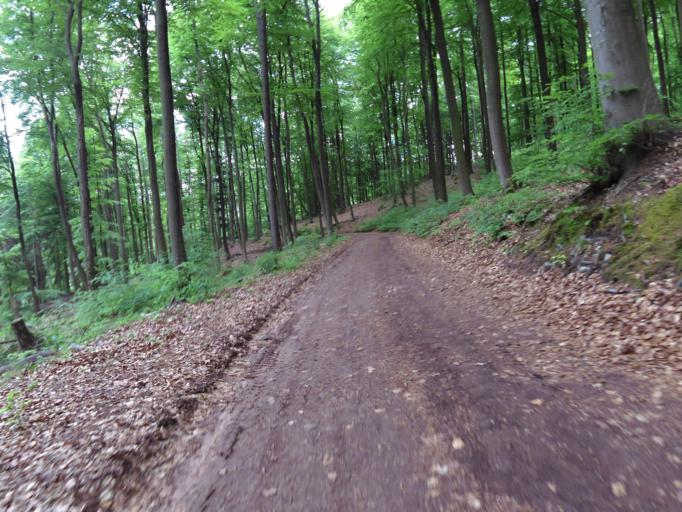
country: DE
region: Rheinland-Pfalz
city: Neidenfels
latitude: 49.4118
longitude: 8.0593
